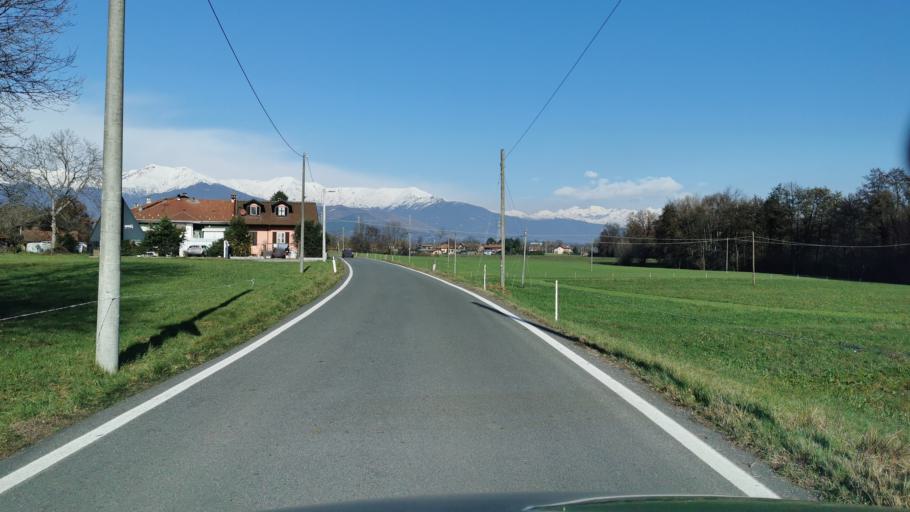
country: IT
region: Piedmont
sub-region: Provincia di Torino
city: Fiano
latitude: 45.2259
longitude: 7.5408
